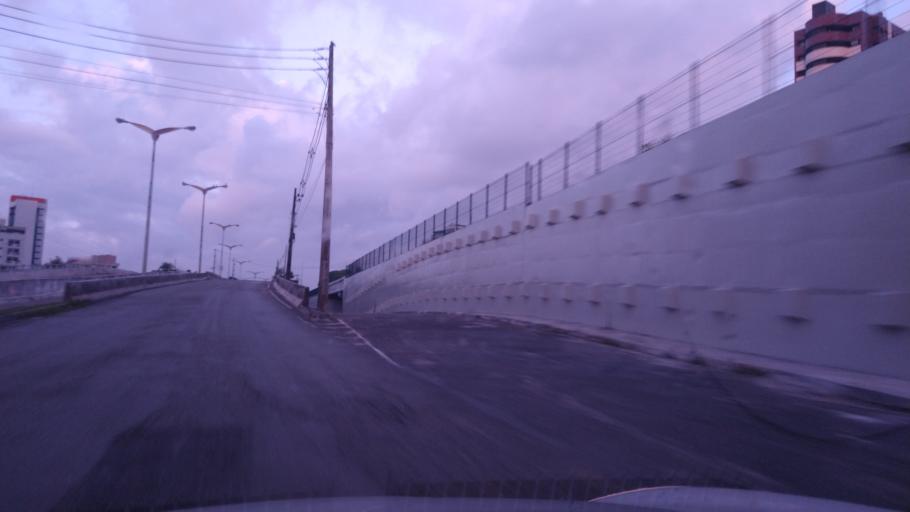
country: BR
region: Ceara
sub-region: Fortaleza
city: Fortaleza
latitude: -3.7475
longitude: -38.4923
